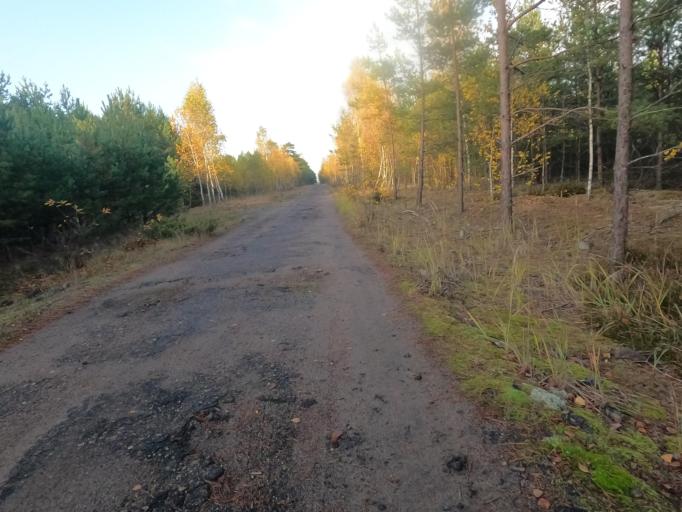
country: PL
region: West Pomeranian Voivodeship
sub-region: Powiat szczecinecki
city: Borne Sulinowo
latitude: 53.5482
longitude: 16.5202
